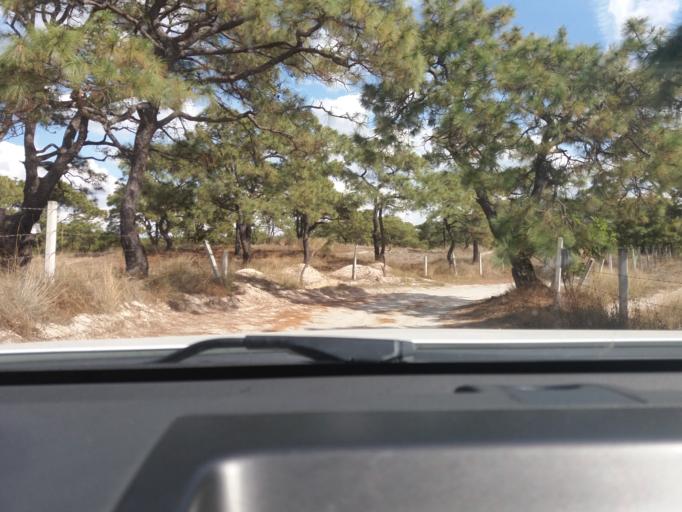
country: MX
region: Jalisco
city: Tala
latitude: 20.6584
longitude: -103.6738
